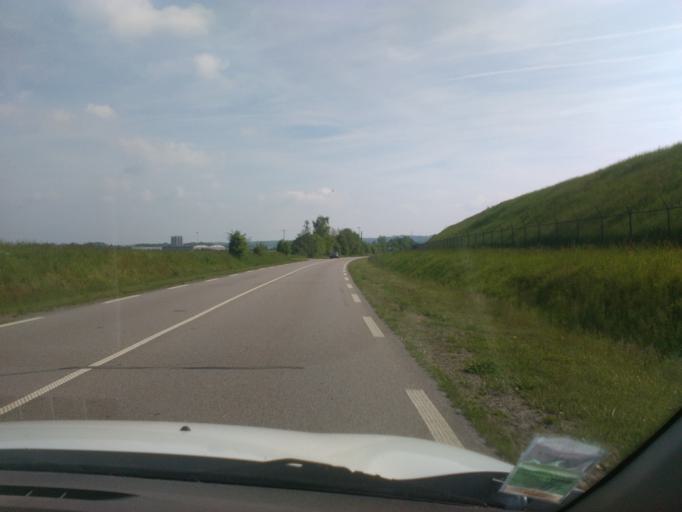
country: FR
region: Lorraine
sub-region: Departement des Vosges
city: Chavelot
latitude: 48.2156
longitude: 6.4223
